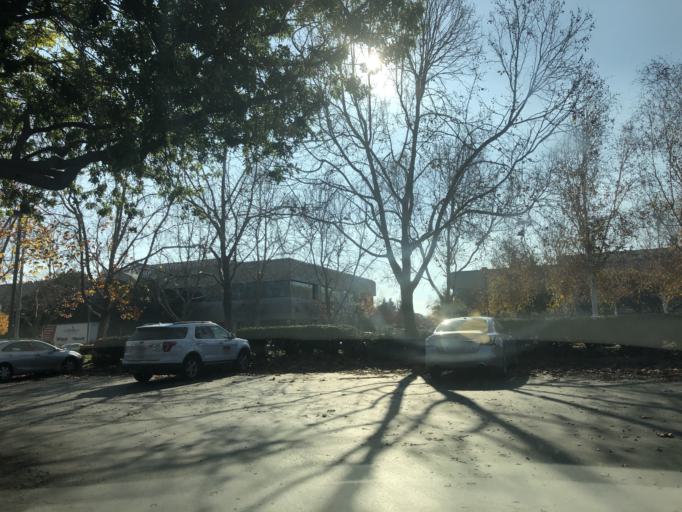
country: US
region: California
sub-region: Santa Clara County
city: Sunnyvale
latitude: 37.3843
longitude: -122.0053
